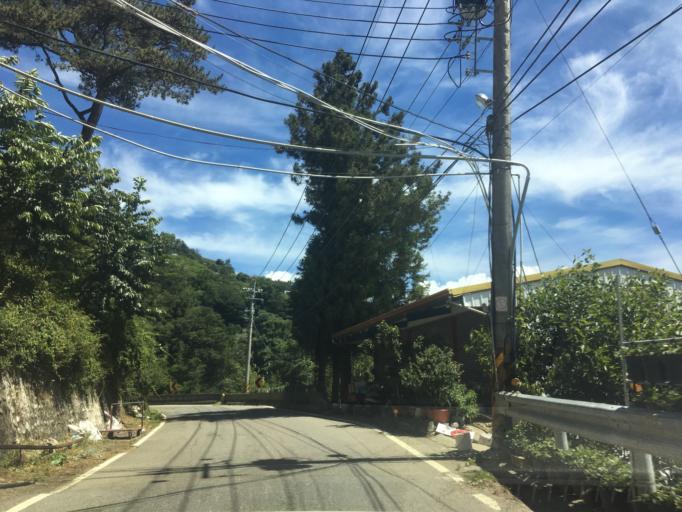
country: TW
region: Taiwan
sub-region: Nantou
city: Puli
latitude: 24.2419
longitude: 121.2555
